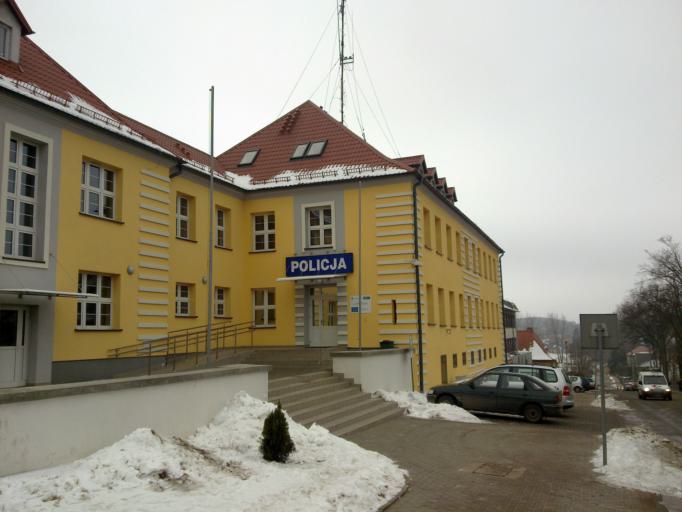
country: PL
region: Pomeranian Voivodeship
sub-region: Powiat bytowski
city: Bytow
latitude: 54.1683
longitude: 17.4995
